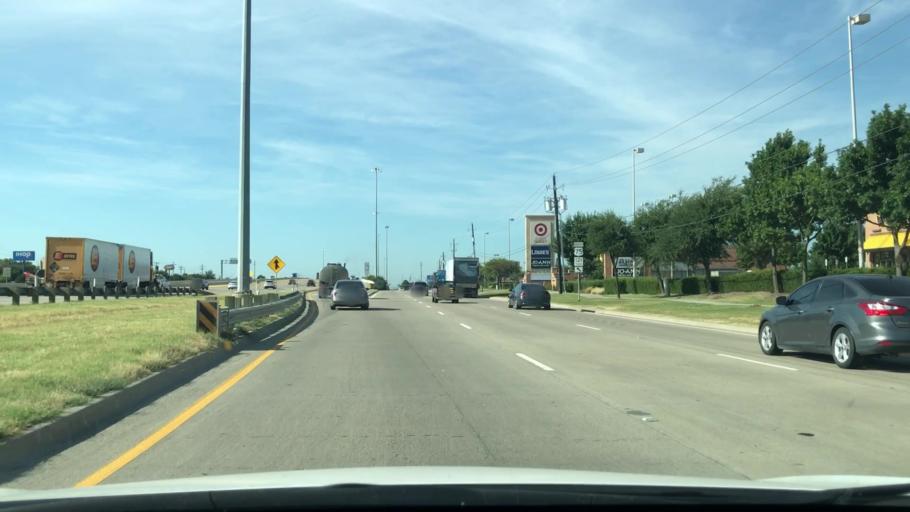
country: US
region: Texas
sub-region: Collin County
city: McKinney
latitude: 33.2217
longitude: -96.6354
